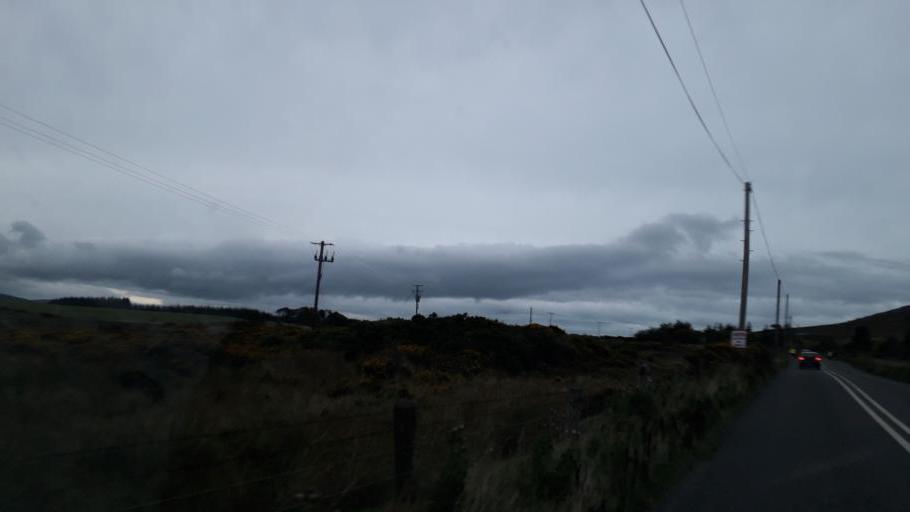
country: IE
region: Leinster
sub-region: Wicklow
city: Kilmacanoge
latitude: 53.1441
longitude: -6.1676
